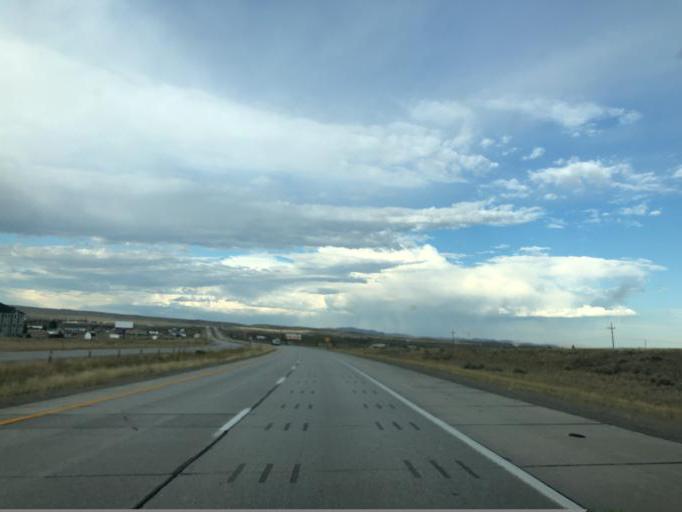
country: US
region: Wyoming
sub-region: Carbon County
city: Rawlins
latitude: 41.7787
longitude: -107.2226
